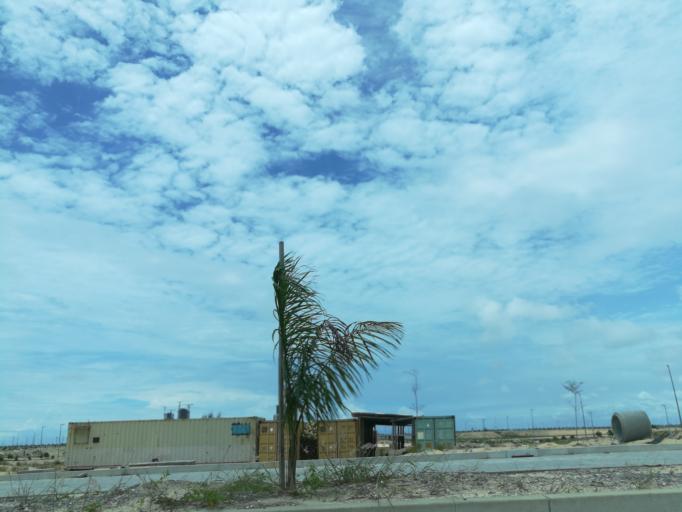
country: NG
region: Lagos
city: Ikoyi
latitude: 6.4154
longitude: 3.4247
